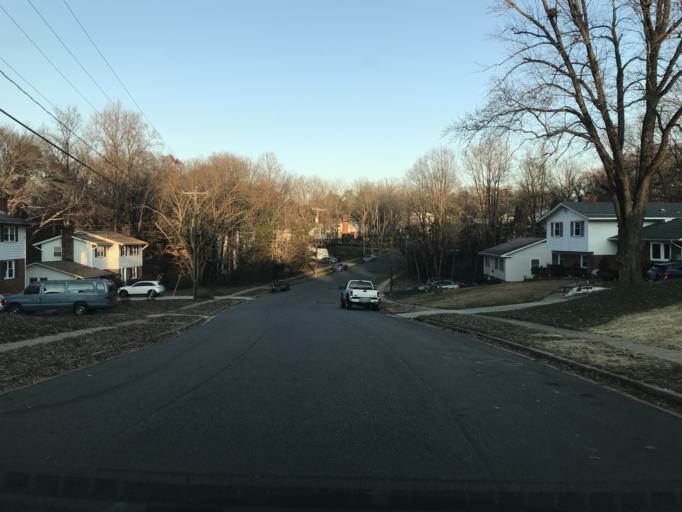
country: US
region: Virginia
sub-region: Fairfax County
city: Springfield
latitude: 38.7876
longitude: -77.1704
